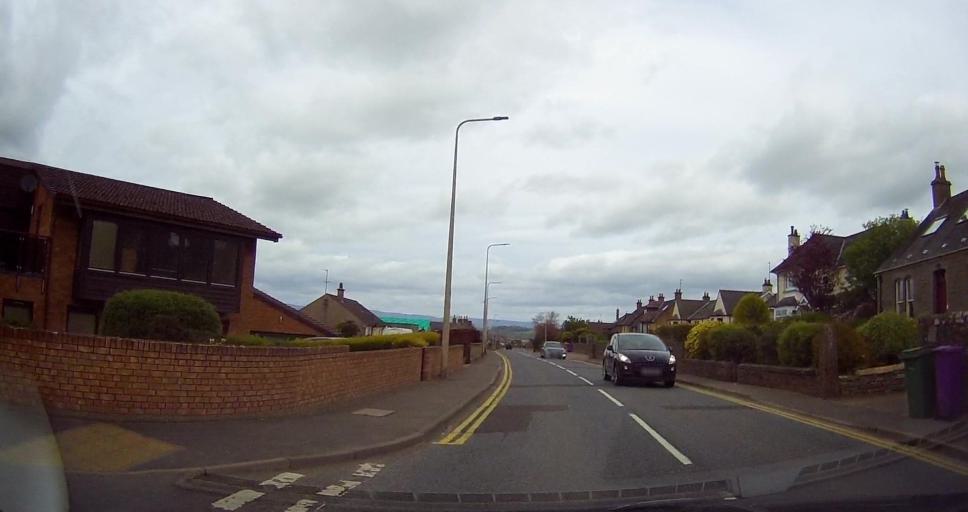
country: GB
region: Scotland
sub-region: Angus
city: Forfar
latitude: 56.6324
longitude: -2.8959
